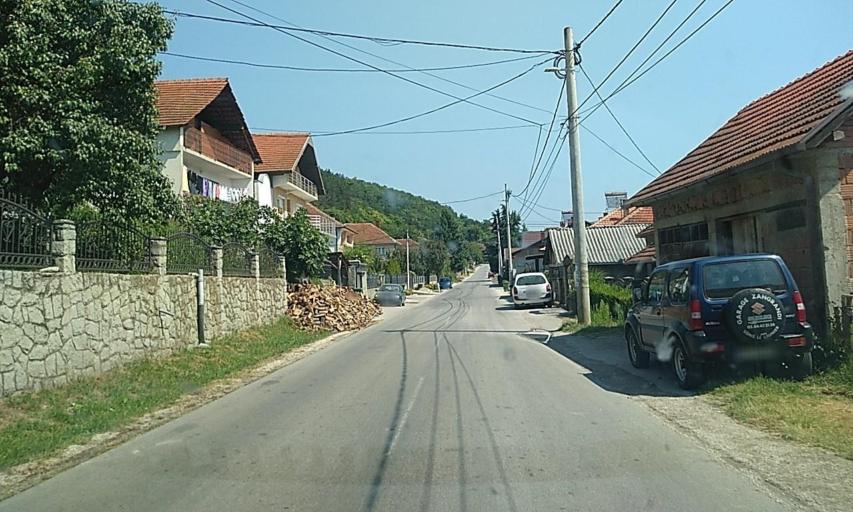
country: RS
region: Central Serbia
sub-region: Pcinjski Okrug
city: Vladicin Han
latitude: 42.6922
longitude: 22.0579
